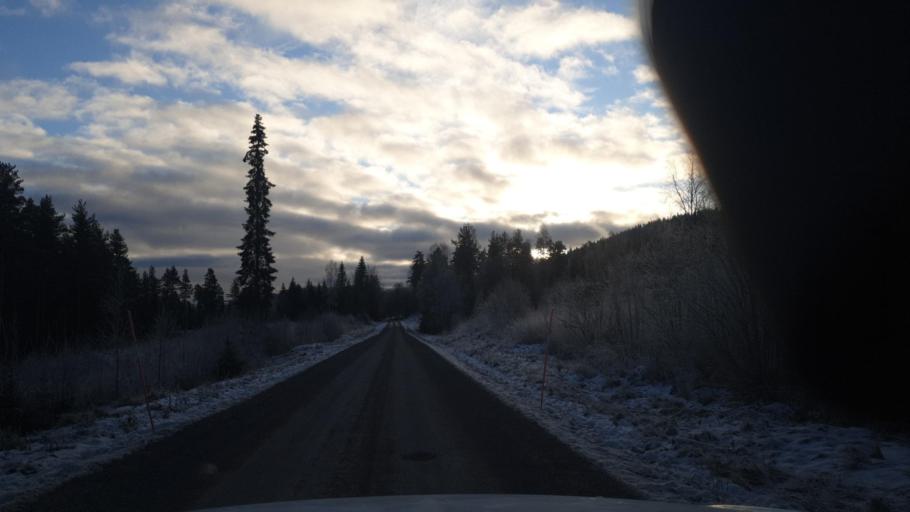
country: SE
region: Vaermland
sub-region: Eda Kommun
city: Charlottenberg
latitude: 60.0798
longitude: 12.5237
